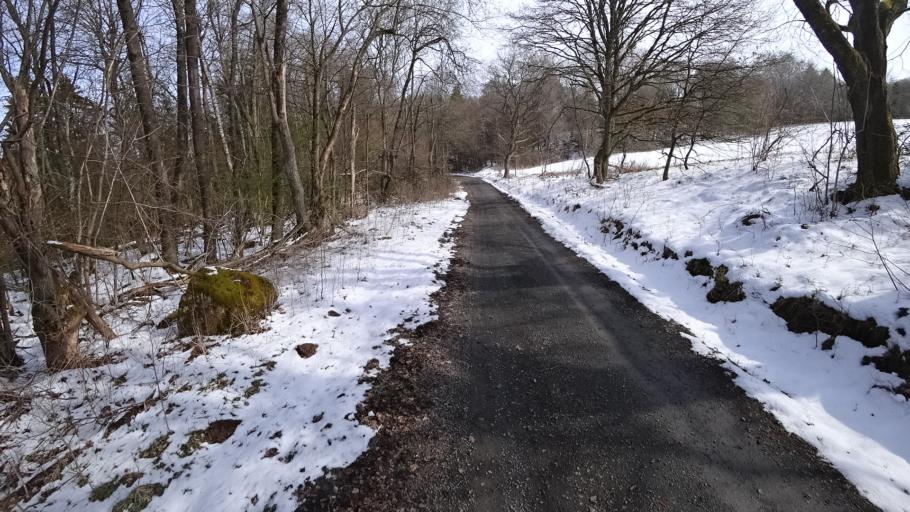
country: DE
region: Rheinland-Pfalz
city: Morlen
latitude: 50.6908
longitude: 7.8794
